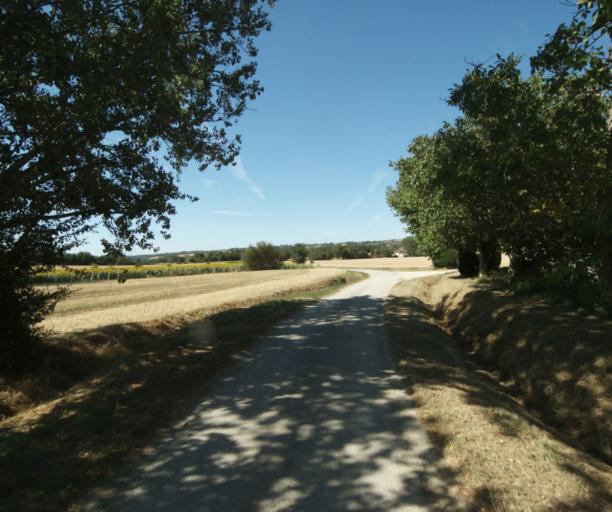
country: FR
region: Midi-Pyrenees
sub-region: Departement de la Haute-Garonne
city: Saint-Felix-Lauragais
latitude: 43.5021
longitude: 1.8952
